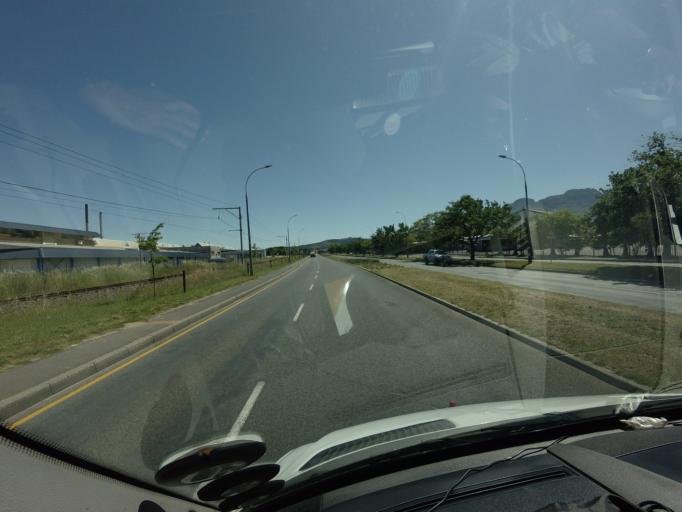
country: ZA
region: Western Cape
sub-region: Cape Winelands District Municipality
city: Stellenbosch
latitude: -33.9293
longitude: 18.8538
